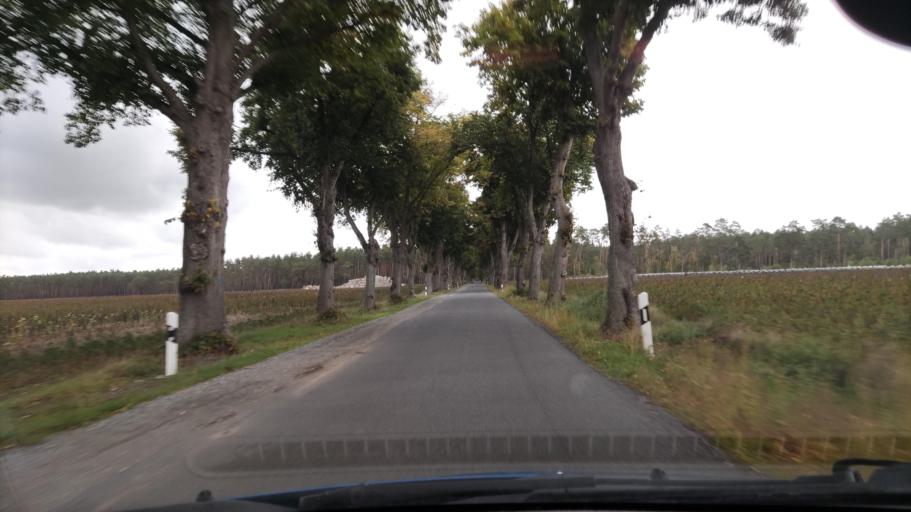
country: DE
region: Saxony-Anhalt
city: Luftkurort Arendsee
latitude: 52.9506
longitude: 11.5441
